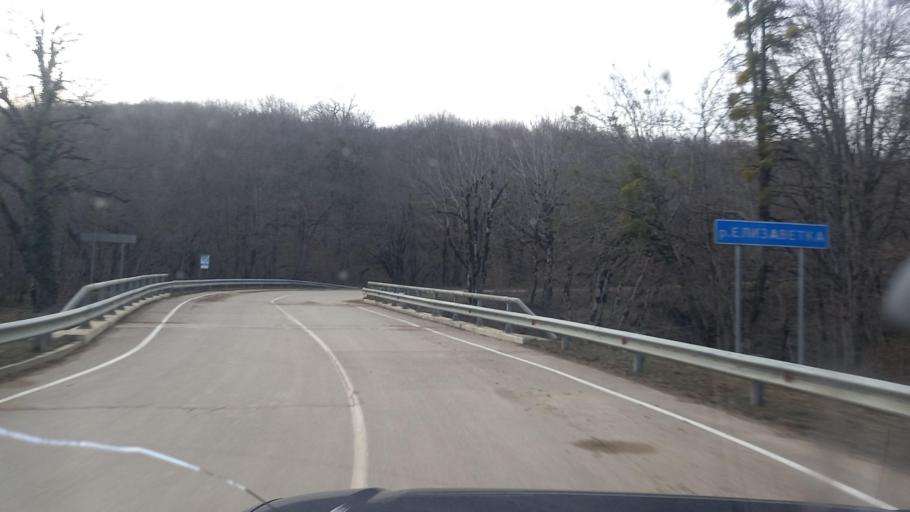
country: RU
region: Krasnodarskiy
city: Khadyzhensk
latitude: 44.3379
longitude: 39.2687
